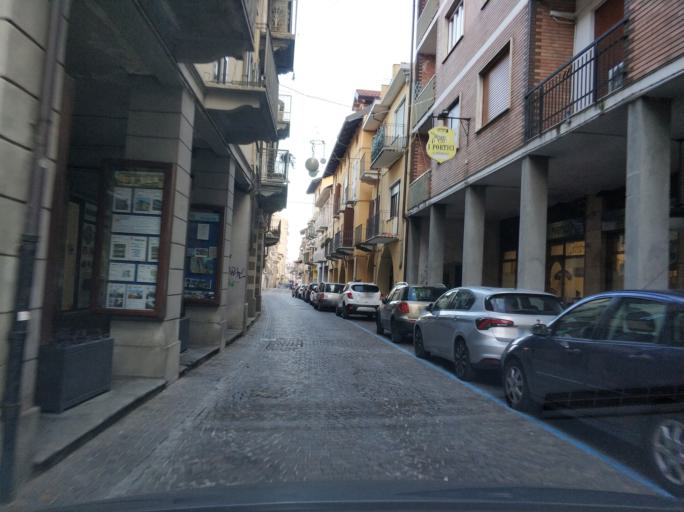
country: IT
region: Piedmont
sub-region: Provincia di Torino
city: Cirie
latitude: 45.2345
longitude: 7.6050
